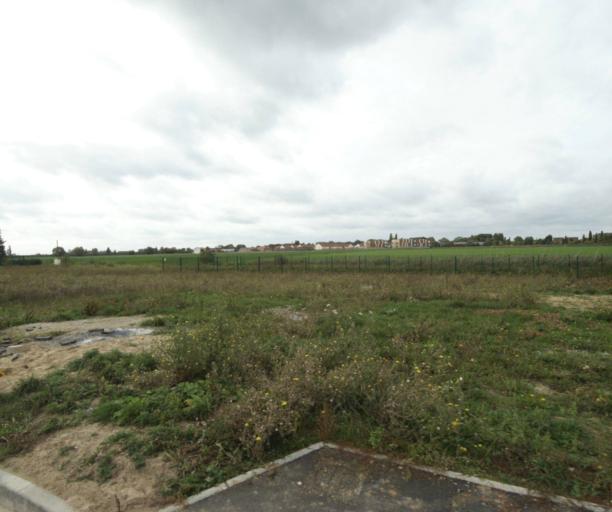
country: FR
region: Nord-Pas-de-Calais
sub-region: Departement du Nord
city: Armentieres
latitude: 50.6780
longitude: 2.8682
